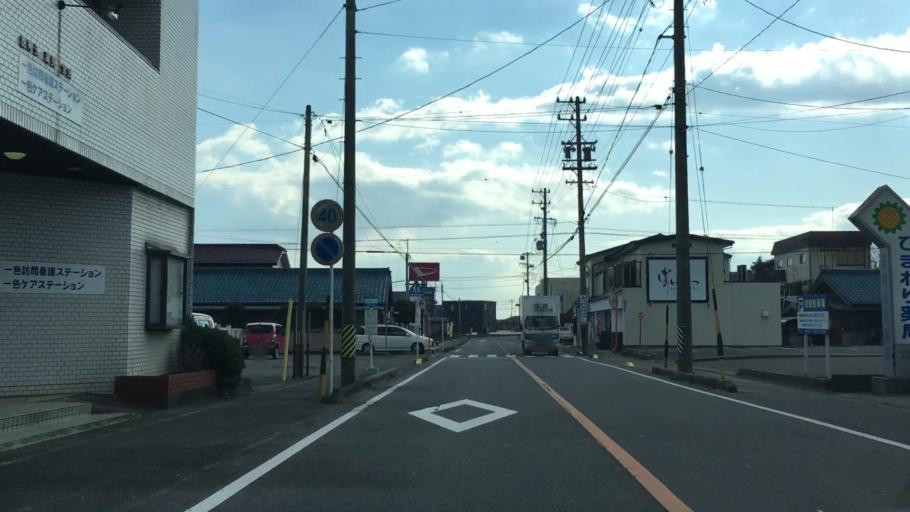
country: JP
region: Aichi
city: Ishiki
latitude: 34.7943
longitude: 137.0413
